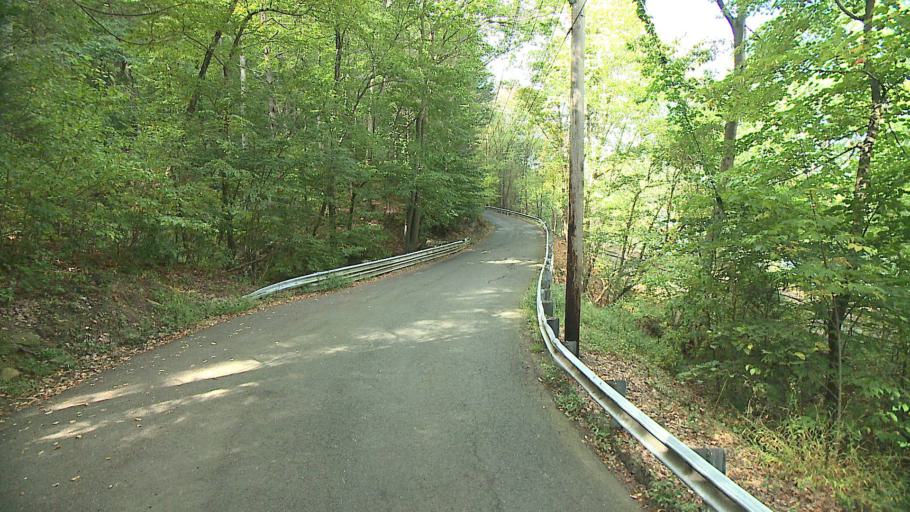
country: US
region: Connecticut
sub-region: Fairfield County
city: Shelton
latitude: 41.3490
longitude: -73.1328
